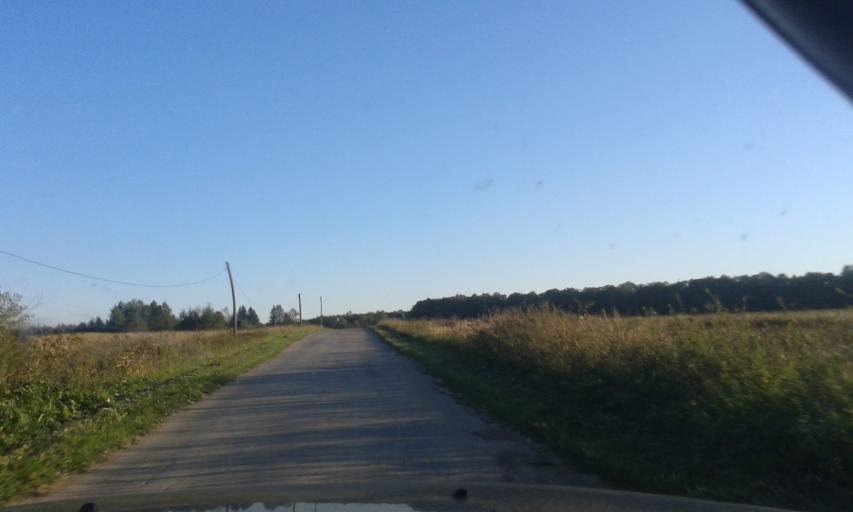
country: RU
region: Tula
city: Krapivna
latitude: 54.1187
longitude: 37.1526
